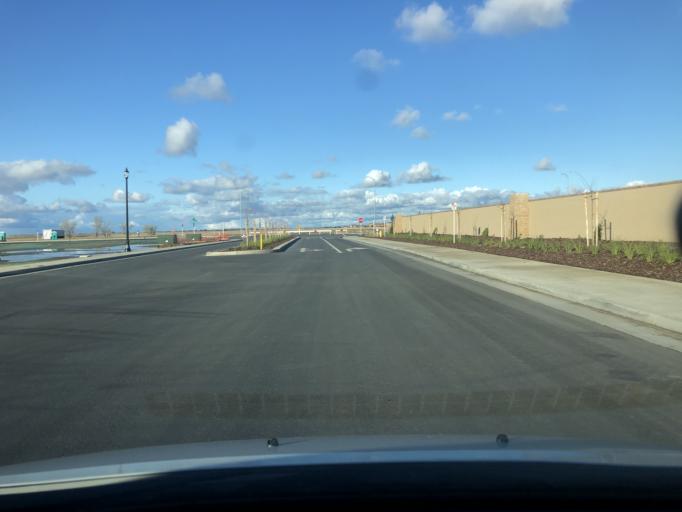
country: US
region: California
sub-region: Sacramento County
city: Elverta
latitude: 38.7741
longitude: -121.3967
